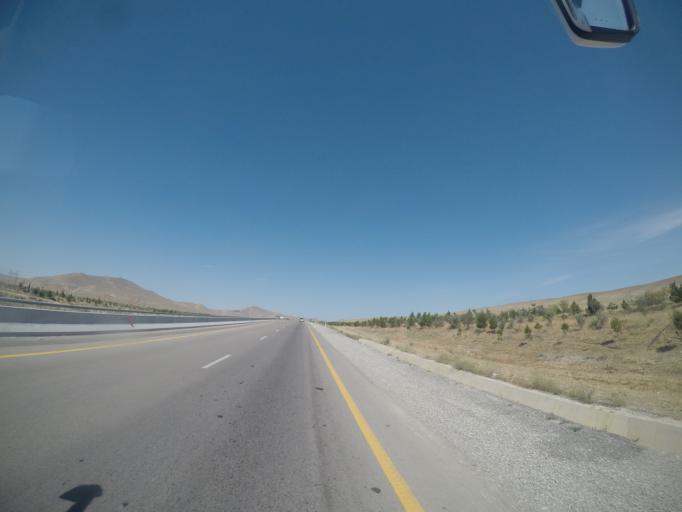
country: AZ
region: Sumqayit
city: Haci Zeynalabdin
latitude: 40.4989
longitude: 49.2978
